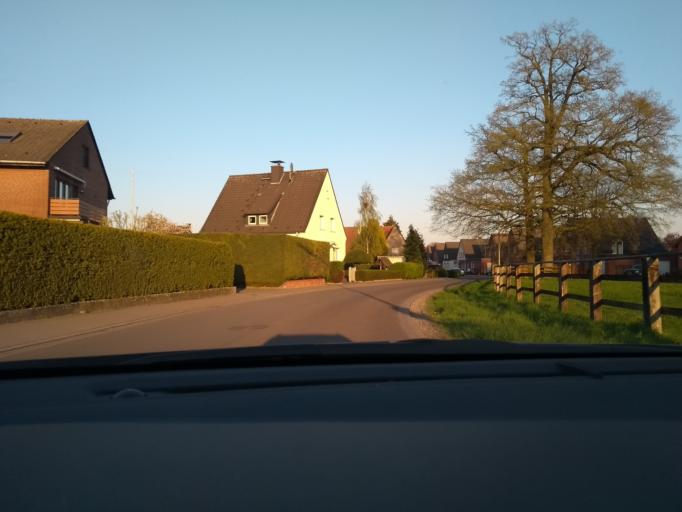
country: DE
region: North Rhine-Westphalia
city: Selm
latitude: 51.6888
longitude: 7.4604
